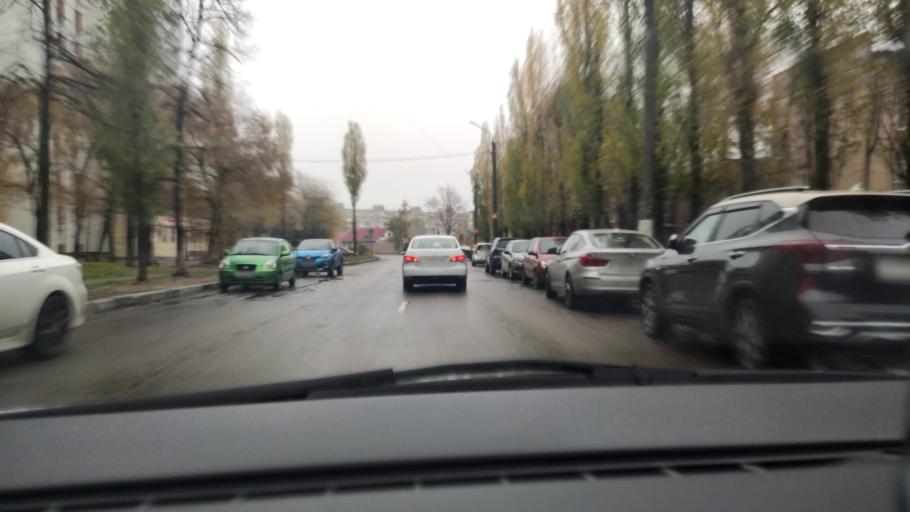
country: RU
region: Voronezj
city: Pridonskoy
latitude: 51.6555
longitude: 39.1178
